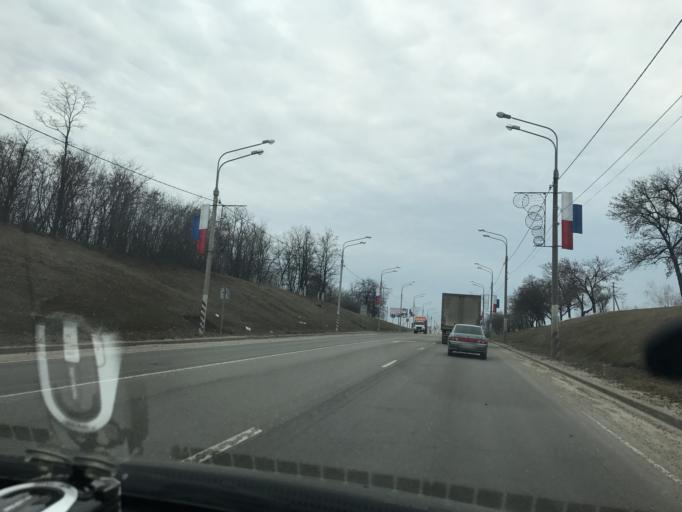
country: RU
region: Krasnodarskiy
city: Kropotkin
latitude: 45.4323
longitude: 40.5359
